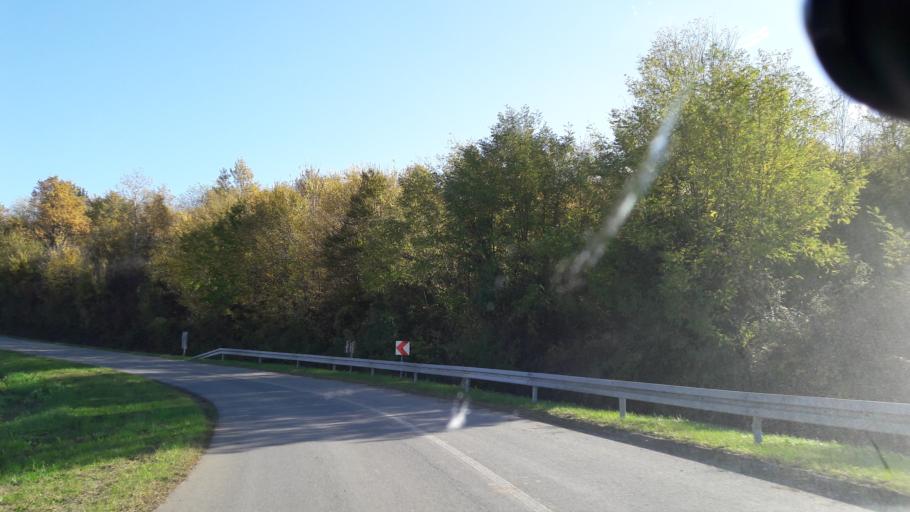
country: HR
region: Osjecko-Baranjska
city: Vukojevci
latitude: 45.3892
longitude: 18.2447
